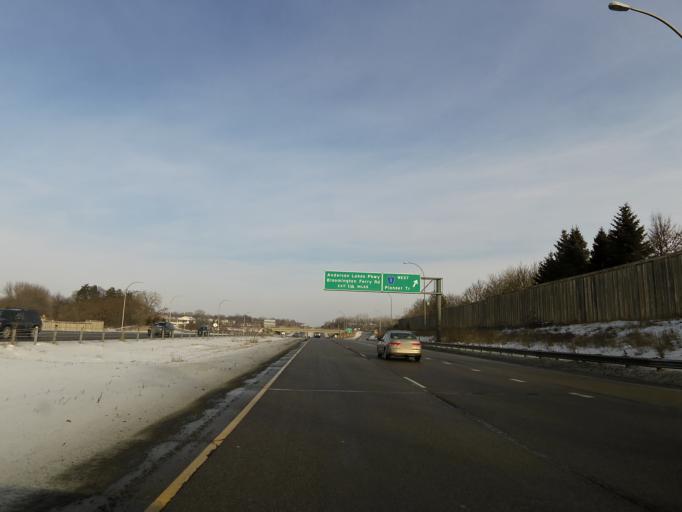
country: US
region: Minnesota
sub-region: Scott County
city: Savage
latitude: 44.8146
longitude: -93.3982
